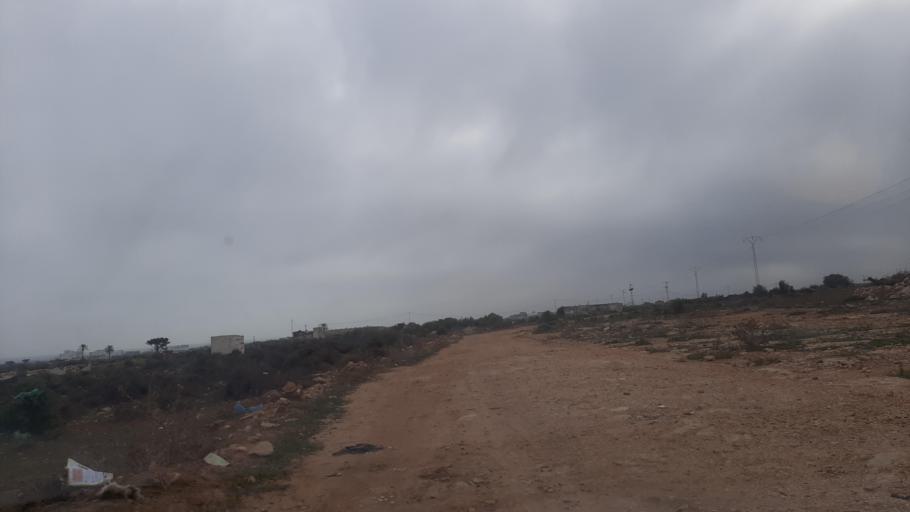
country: TN
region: Nabul
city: Menzel Heurr
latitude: 36.6920
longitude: 10.9350
